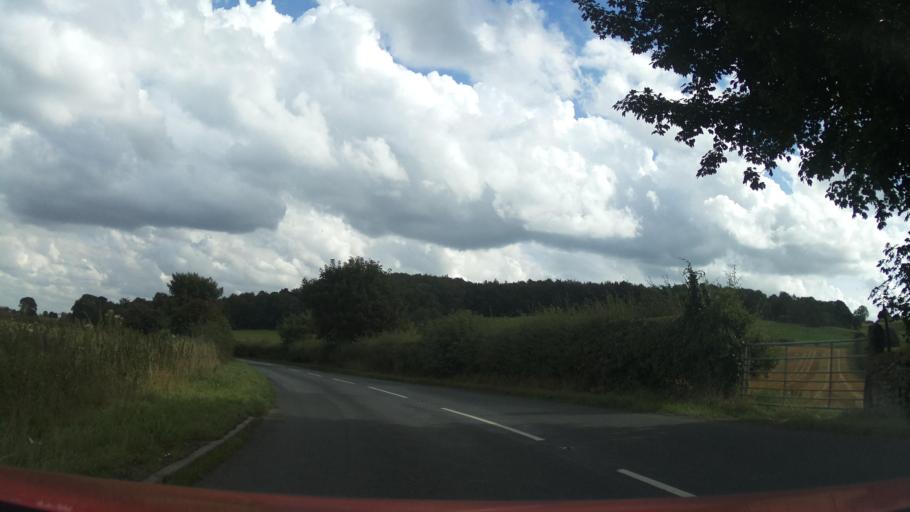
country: GB
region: England
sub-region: North Yorkshire
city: Leyburn
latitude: 54.2590
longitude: -1.7248
